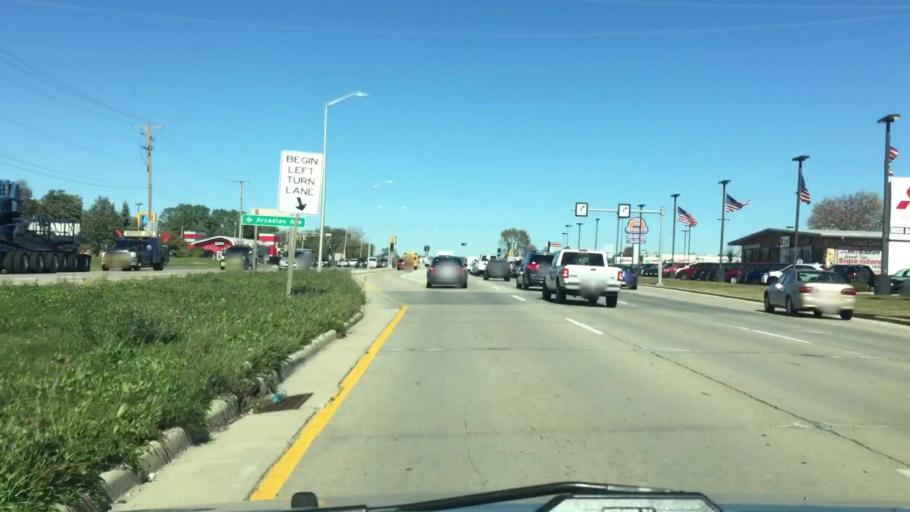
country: US
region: Wisconsin
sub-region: Waukesha County
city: Waukesha
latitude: 43.0122
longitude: -88.2002
